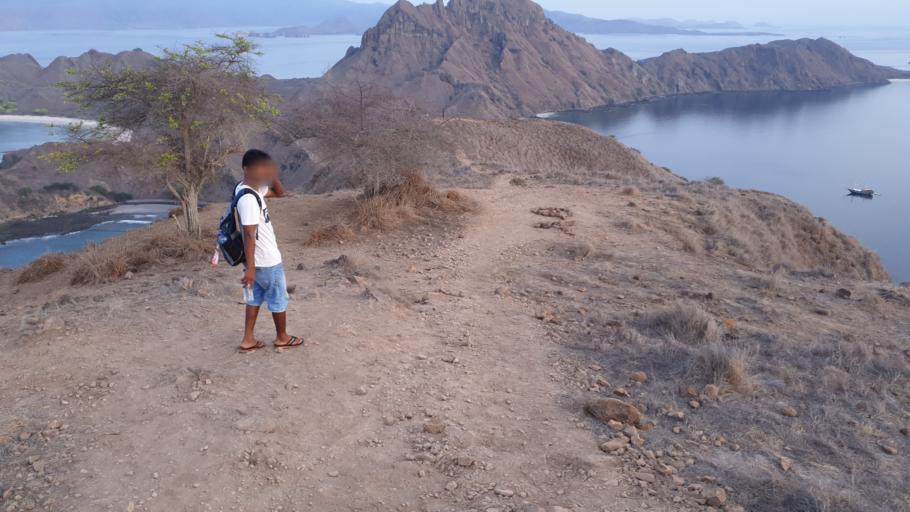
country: ID
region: East Nusa Tenggara
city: Komodo
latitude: -8.6837
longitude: 119.5575
